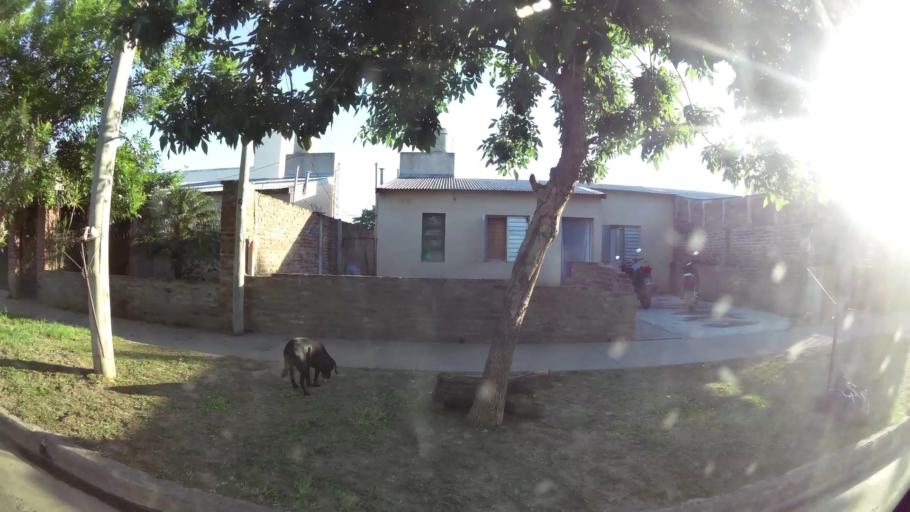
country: AR
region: Santa Fe
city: Santa Fe de la Vera Cruz
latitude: -31.5921
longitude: -60.6831
